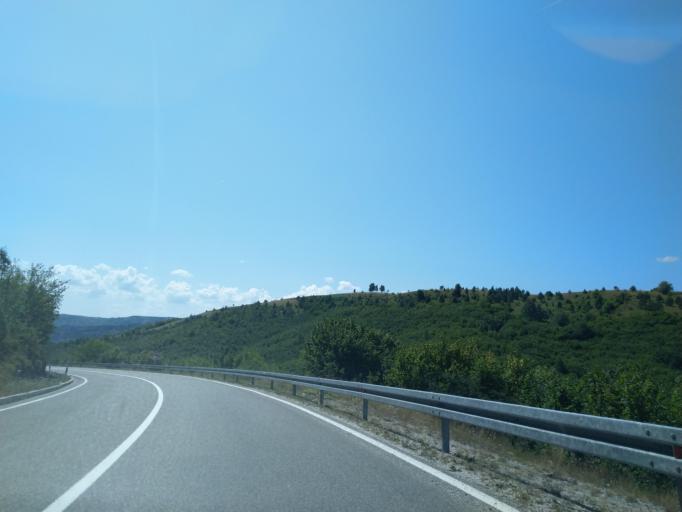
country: RS
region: Central Serbia
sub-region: Zlatiborski Okrug
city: Sjenica
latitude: 43.3023
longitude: 19.9298
